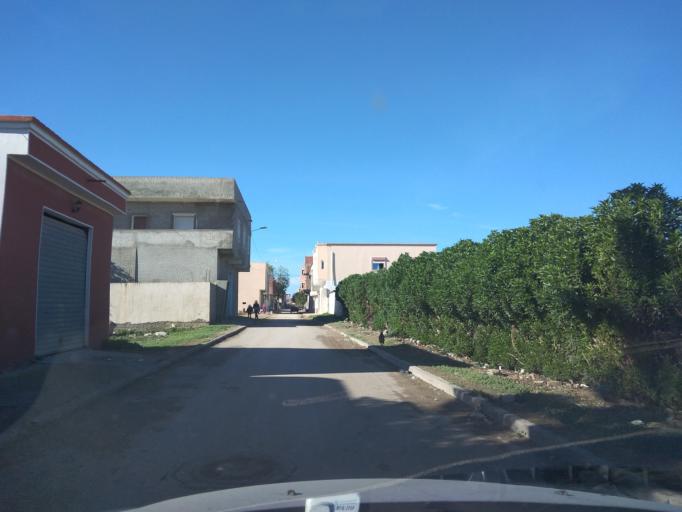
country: TN
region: Ariana
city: Qal'at al Andalus
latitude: 37.0641
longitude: 10.1244
